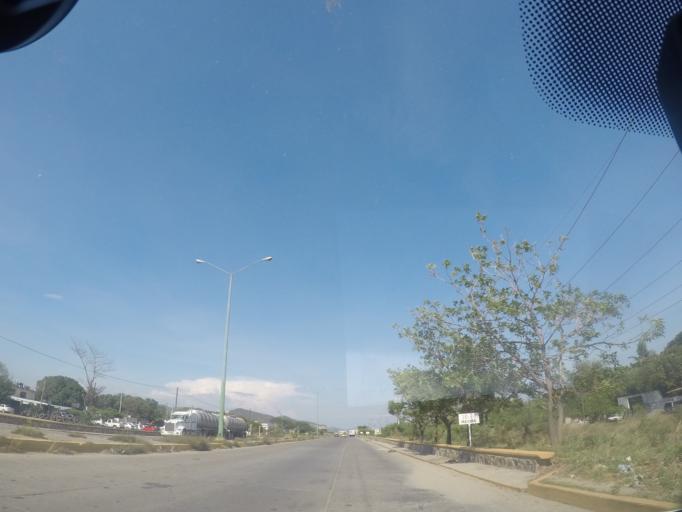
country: MX
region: Oaxaca
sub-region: Salina Cruz
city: Salina Cruz
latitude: 16.2207
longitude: -95.2002
